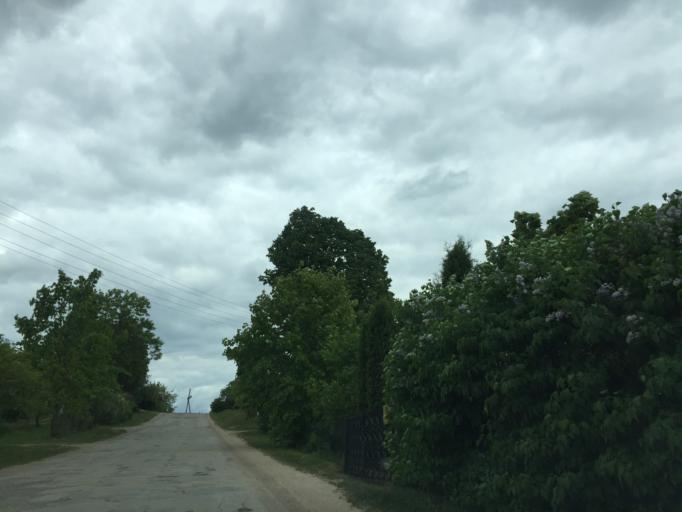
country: LV
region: Dagda
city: Dagda
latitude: 55.9746
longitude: 27.6035
